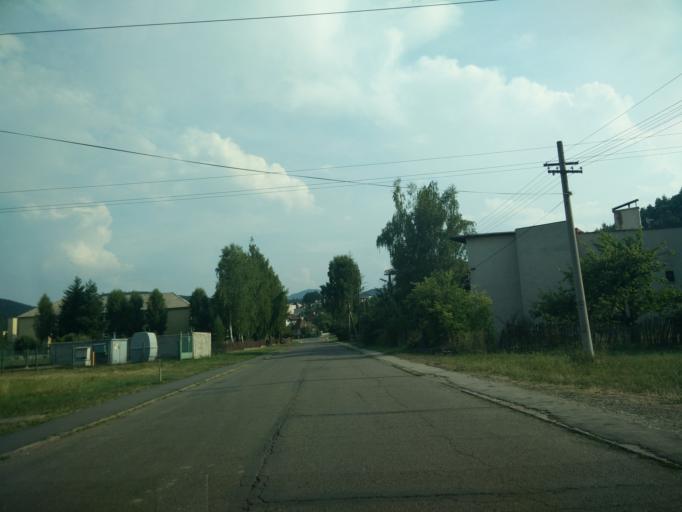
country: SK
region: Banskobystricky
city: Ziar nad Hronom
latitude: 48.5383
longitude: 18.7852
